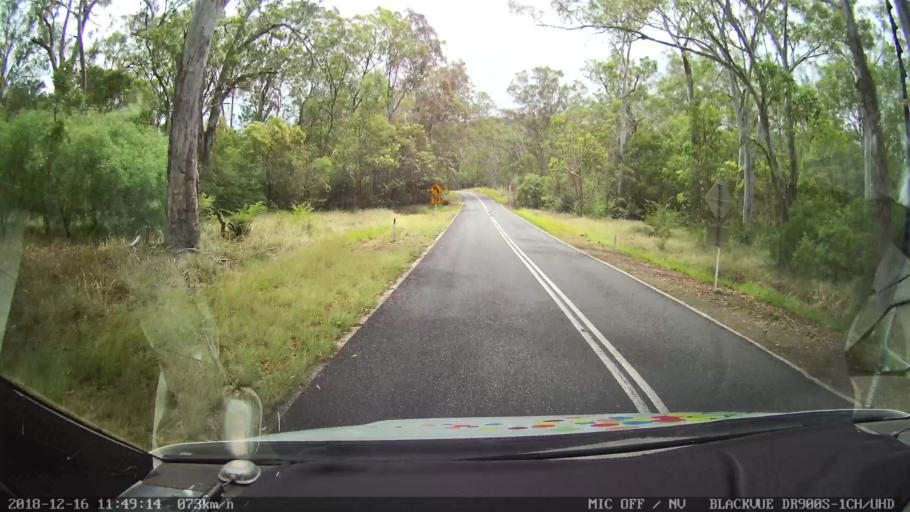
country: AU
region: New South Wales
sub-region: Tenterfield Municipality
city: Carrolls Creek
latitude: -28.9161
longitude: 152.2546
